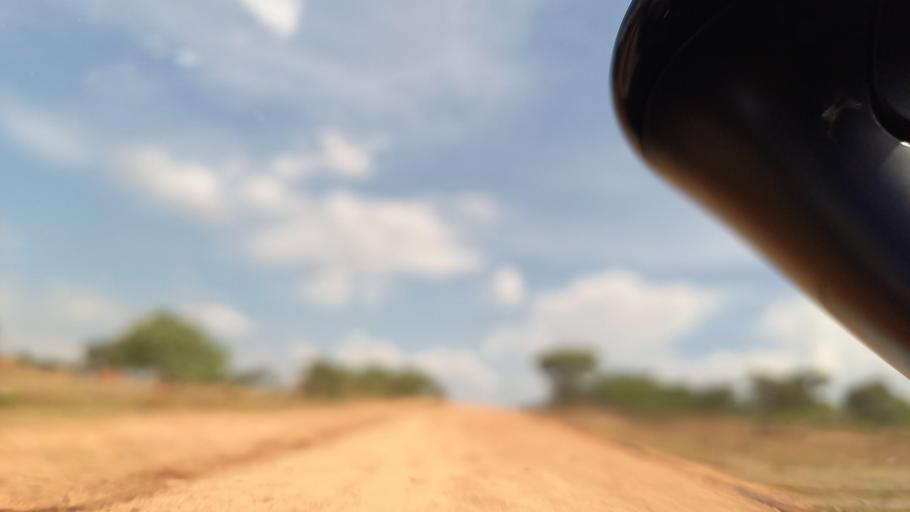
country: ZM
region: Lusaka
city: Kafue
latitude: -16.1290
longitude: 28.0462
